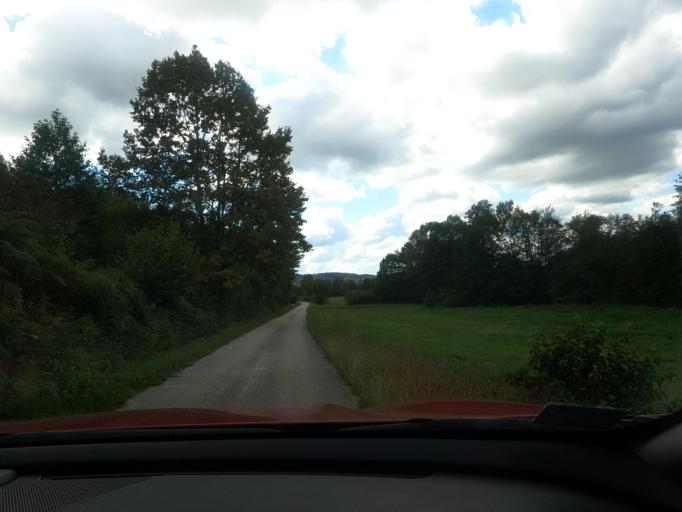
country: BA
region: Federation of Bosnia and Herzegovina
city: Velika Kladusa
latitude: 45.2205
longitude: 15.7101
